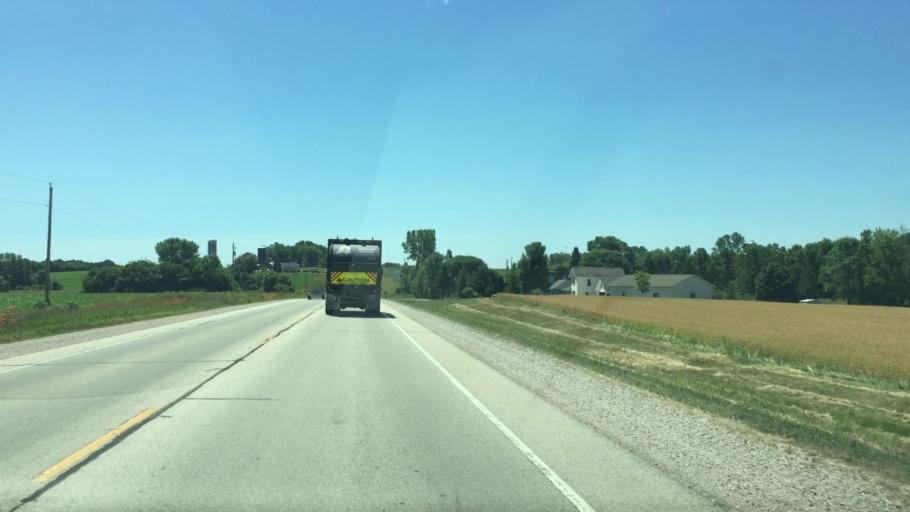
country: US
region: Wisconsin
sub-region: Calumet County
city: Chilton
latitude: 44.0637
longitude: -88.1632
